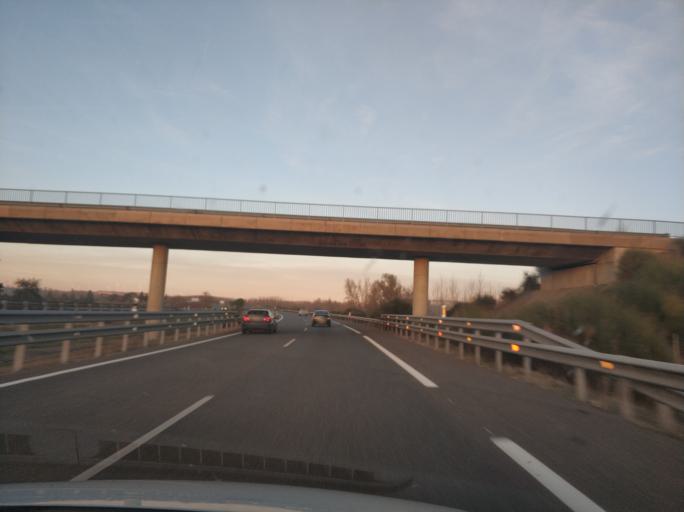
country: ES
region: Castille and Leon
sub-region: Provincia de Palencia
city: Venta de Banos
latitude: 41.9252
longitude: -4.5014
